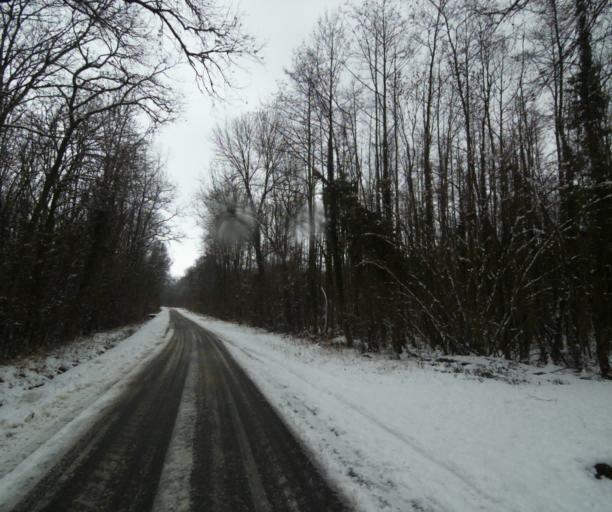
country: FR
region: Champagne-Ardenne
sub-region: Departement de la Haute-Marne
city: Wassy
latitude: 48.4545
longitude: 4.9420
